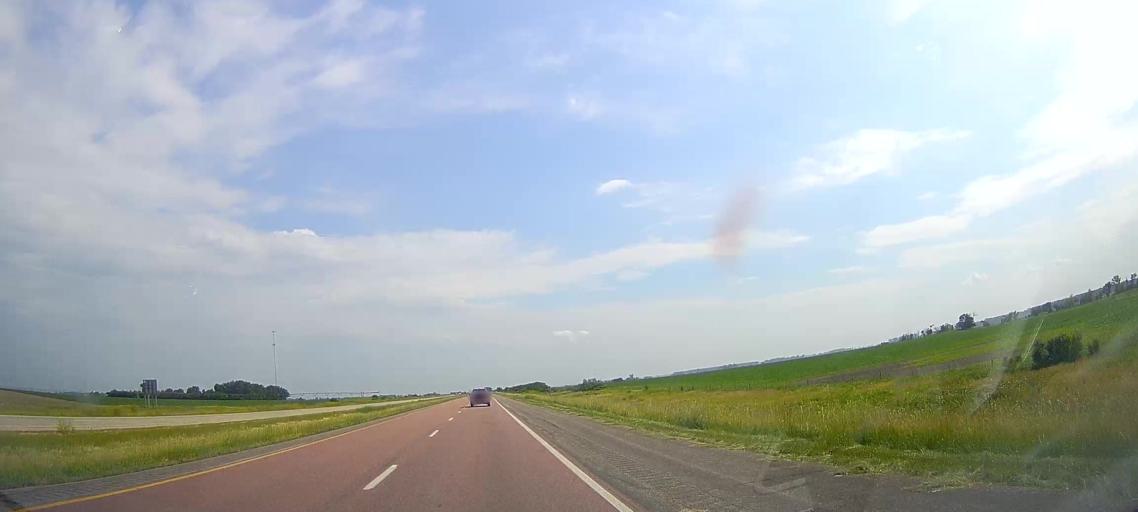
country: US
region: Iowa
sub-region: Monona County
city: Onawa
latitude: 41.9621
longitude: -96.1029
